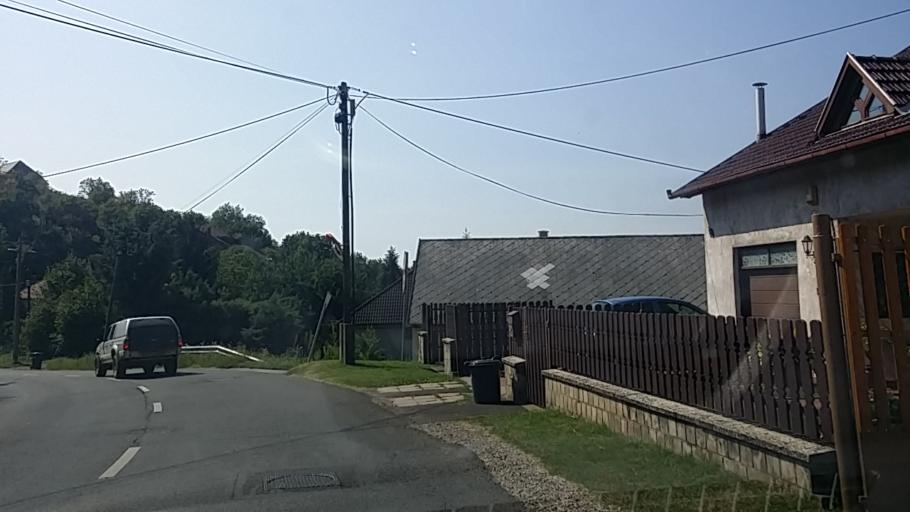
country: HU
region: Baranya
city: Pecs
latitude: 46.0909
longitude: 18.1864
